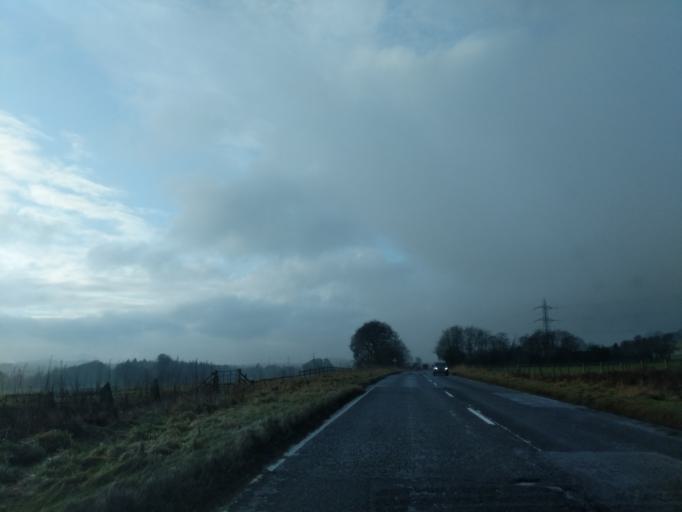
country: GB
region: Scotland
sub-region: Fife
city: Saline
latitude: 56.1942
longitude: -3.5203
